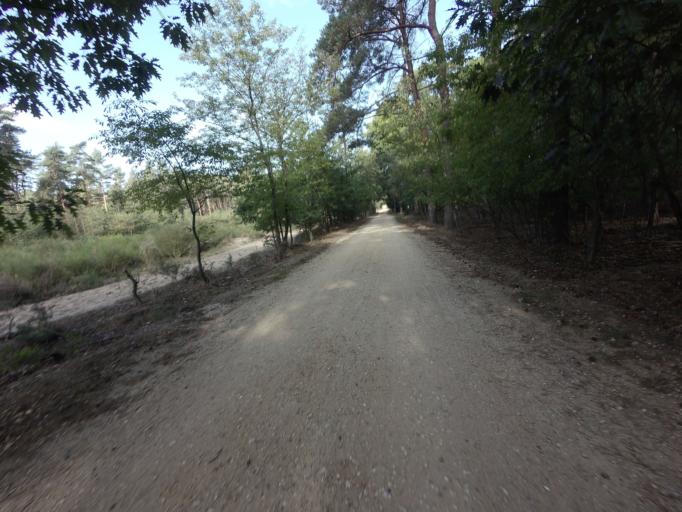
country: NL
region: Limburg
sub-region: Gemeente Roerdalen
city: Herkenbosch
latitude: 51.1776
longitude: 6.0781
